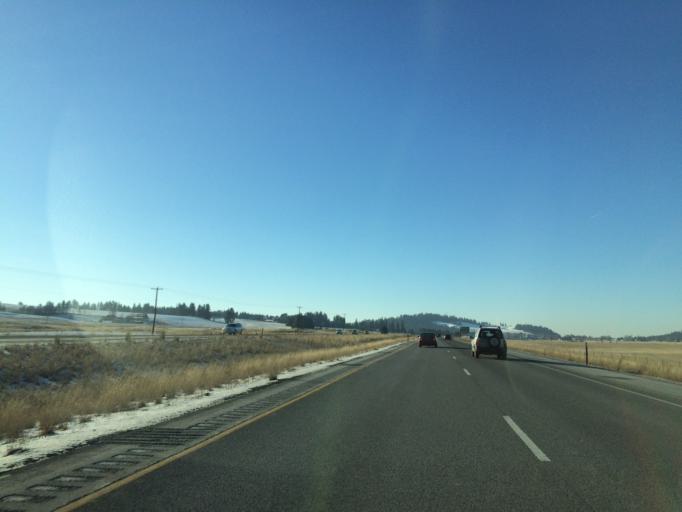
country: US
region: Washington
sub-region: Spokane County
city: Airway Heights
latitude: 47.5769
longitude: -117.5813
